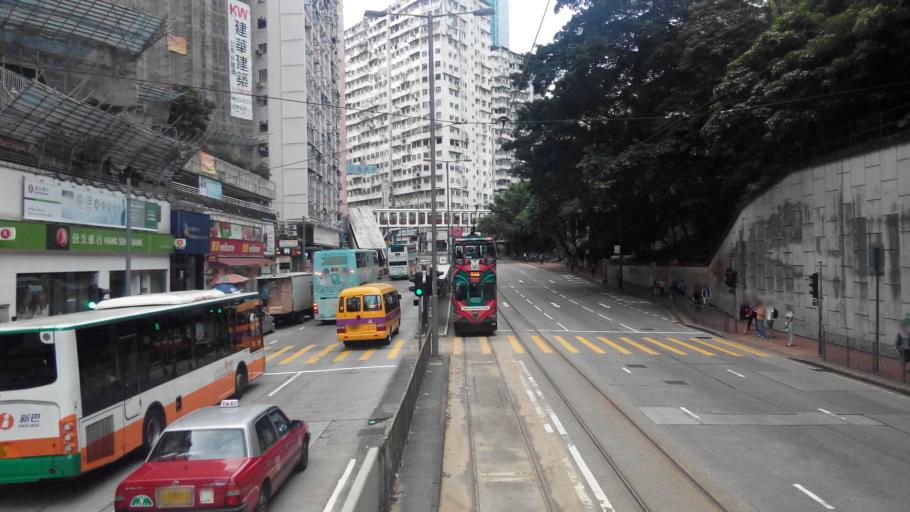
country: HK
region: Wanchai
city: Wan Chai
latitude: 22.2861
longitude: 114.2109
